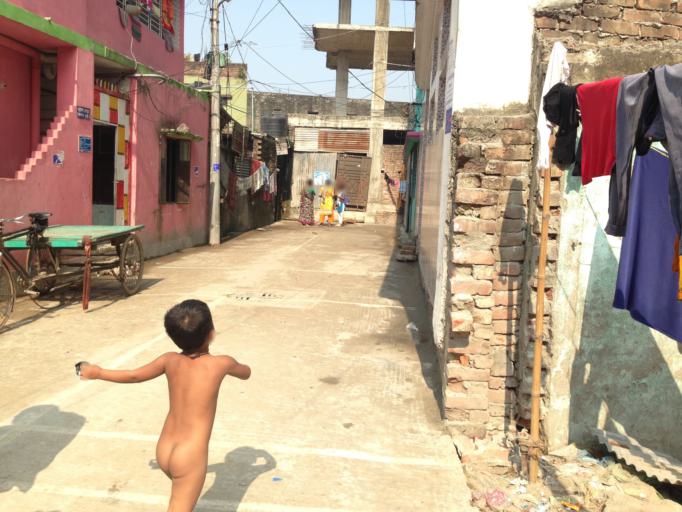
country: BD
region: Dhaka
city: Azimpur
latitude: 23.8029
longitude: 90.3457
